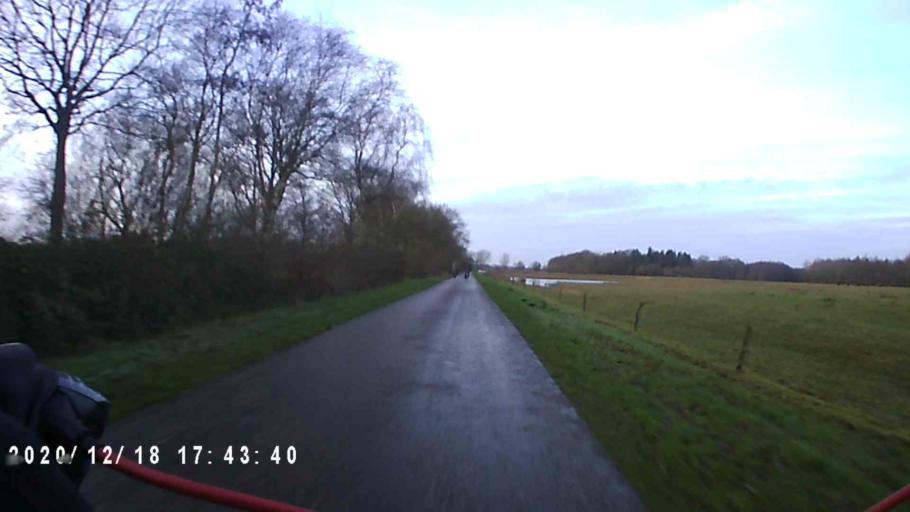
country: NL
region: Drenthe
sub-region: Gemeente Tynaarlo
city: Vries
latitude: 53.1053
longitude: 6.5707
